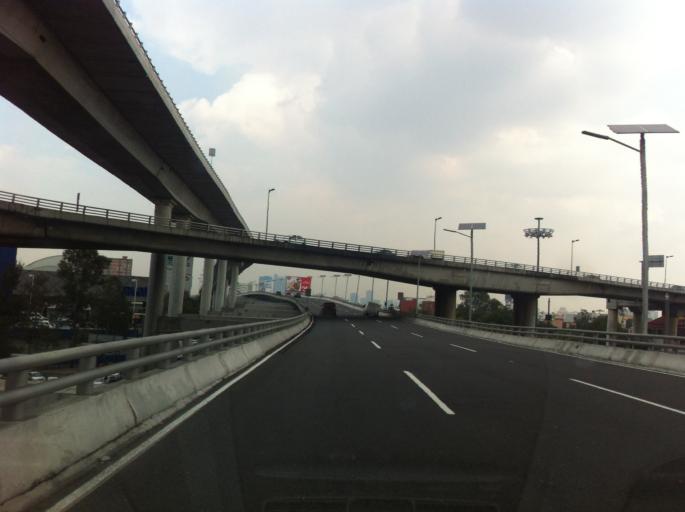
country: MX
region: Mexico City
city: Alvaro Obregon
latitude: 19.3841
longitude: -99.1913
